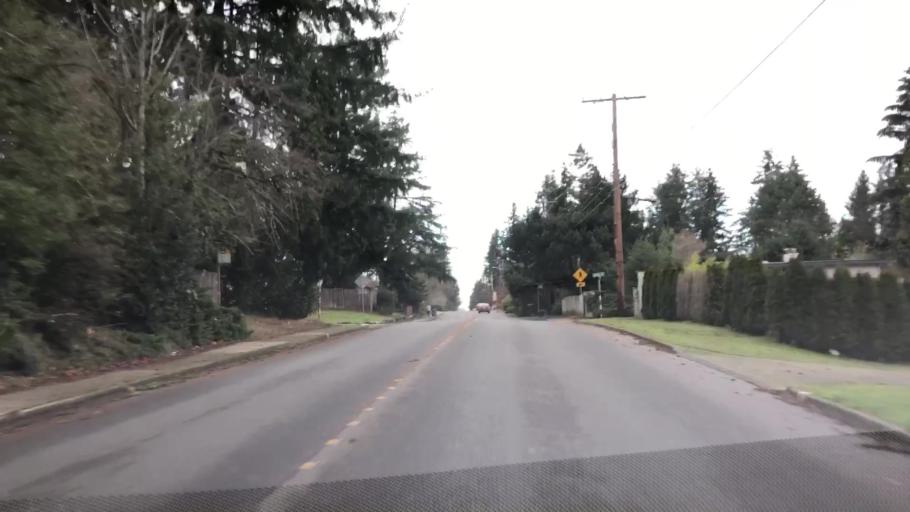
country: US
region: Washington
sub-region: King County
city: West Lake Sammamish
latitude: 47.6093
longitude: -122.1213
